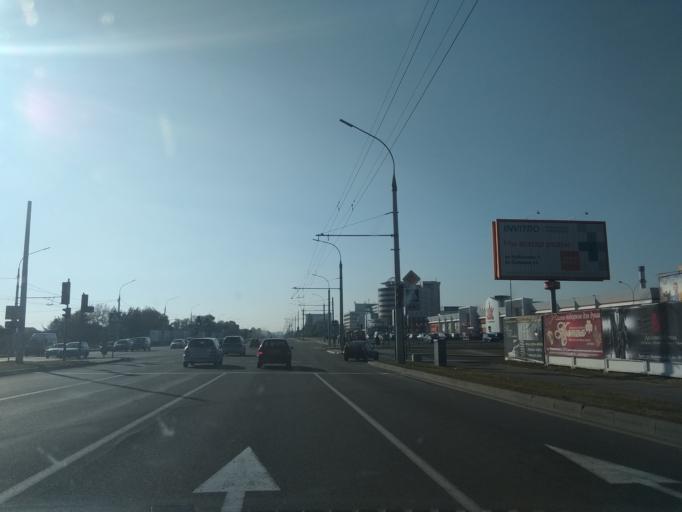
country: BY
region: Brest
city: Brest
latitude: 52.0966
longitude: 23.7477
